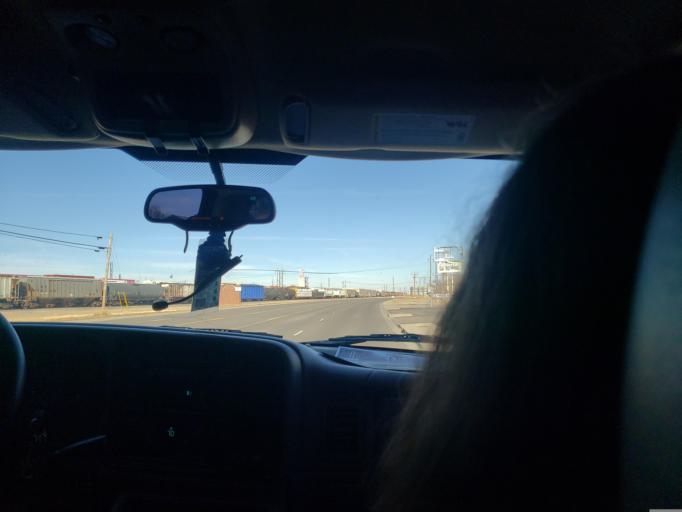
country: US
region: Texas
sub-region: Dallam County
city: Dalhart
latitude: 36.0742
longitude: -102.5072
